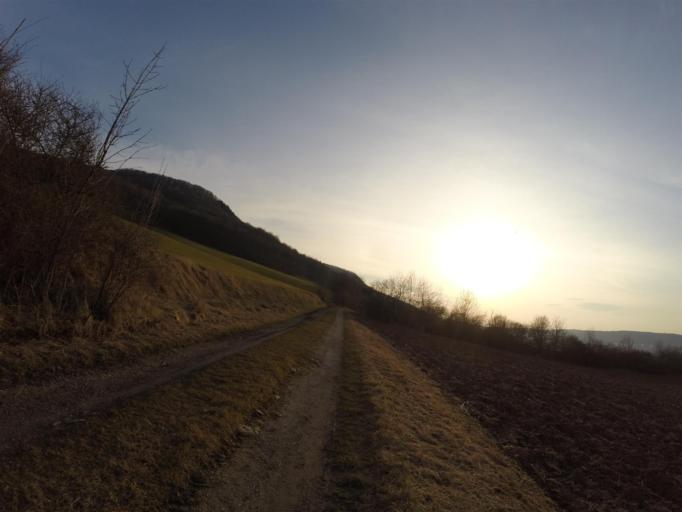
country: DE
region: Thuringia
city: Golmsdorf
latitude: 50.9471
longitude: 11.6366
